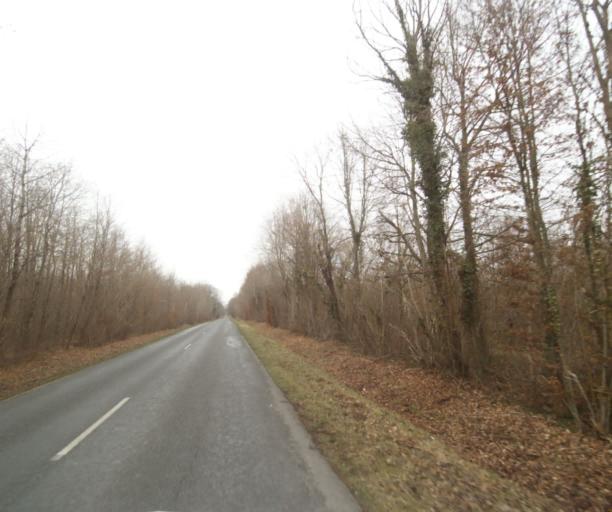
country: FR
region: Champagne-Ardenne
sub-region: Departement de la Marne
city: Pargny-sur-Saulx
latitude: 48.7233
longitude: 4.8734
